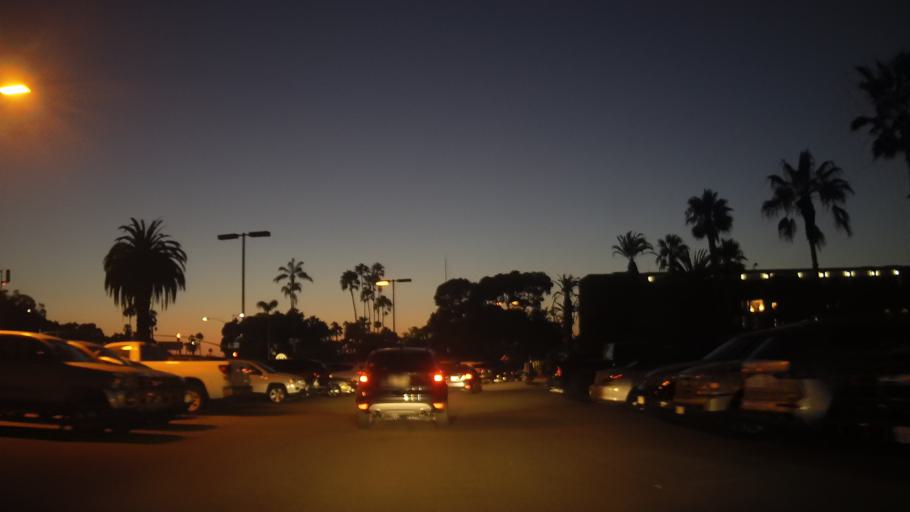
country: US
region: California
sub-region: San Diego County
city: La Jolla
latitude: 32.7708
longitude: -117.2455
